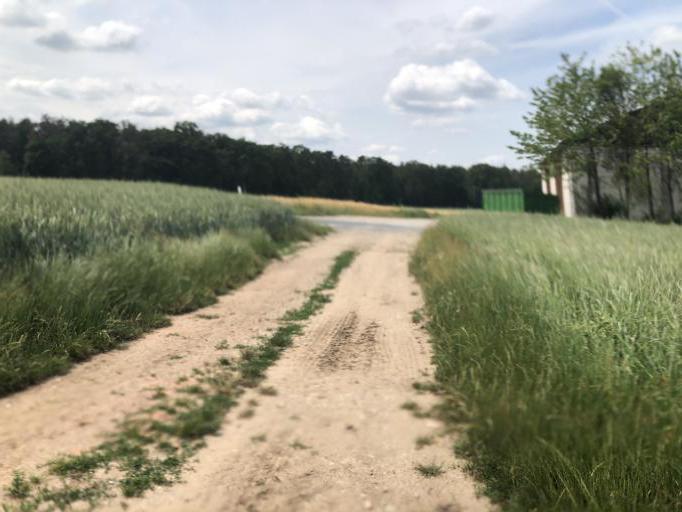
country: DE
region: Bavaria
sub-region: Regierungsbezirk Mittelfranken
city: Herzogenaurach
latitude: 49.5758
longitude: 10.9379
